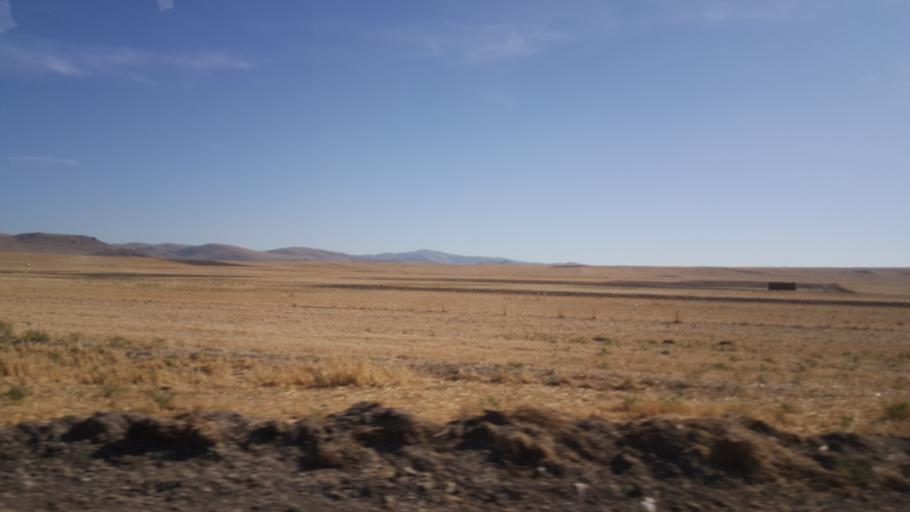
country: TR
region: Ankara
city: Yenice
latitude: 39.3434
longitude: 32.7513
